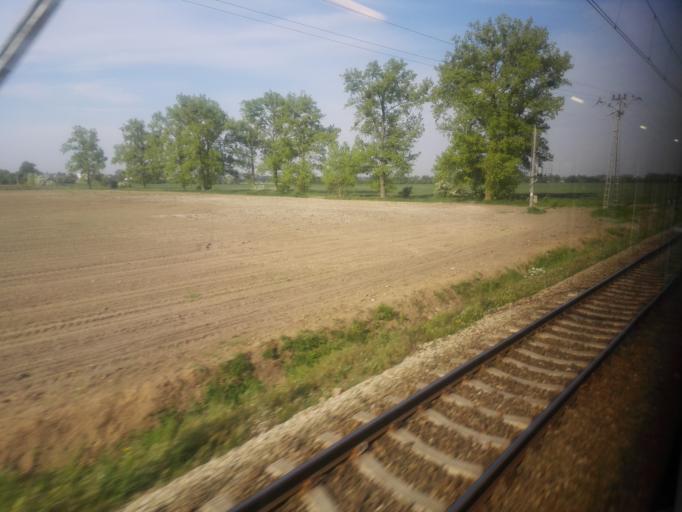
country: PL
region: Greater Poland Voivodeship
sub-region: Powiat wrzesinski
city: Wrzesnia
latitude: 52.3353
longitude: 17.6133
